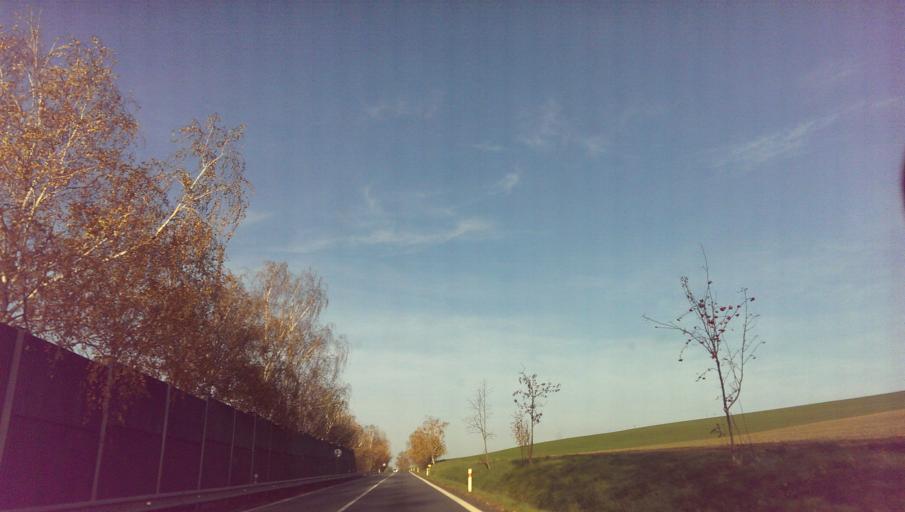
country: CZ
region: Zlin
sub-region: Okres Zlin
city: Ostrozska Nova Ves
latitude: 49.0185
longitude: 17.4471
